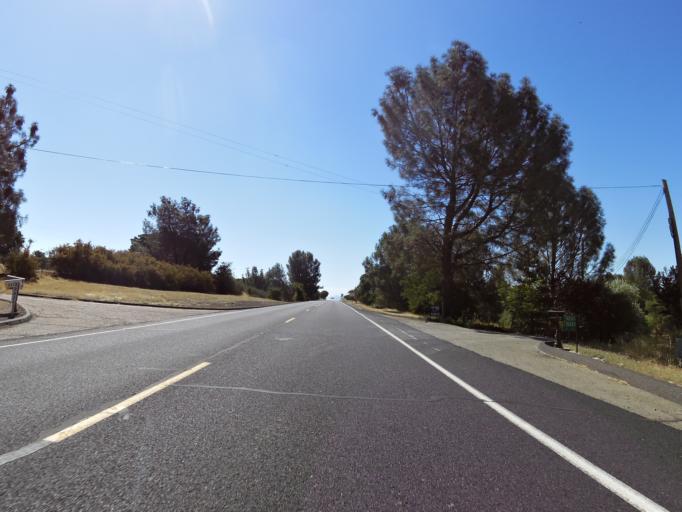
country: US
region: California
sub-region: Tuolumne County
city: Tuolumne City
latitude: 37.7122
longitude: -120.3167
